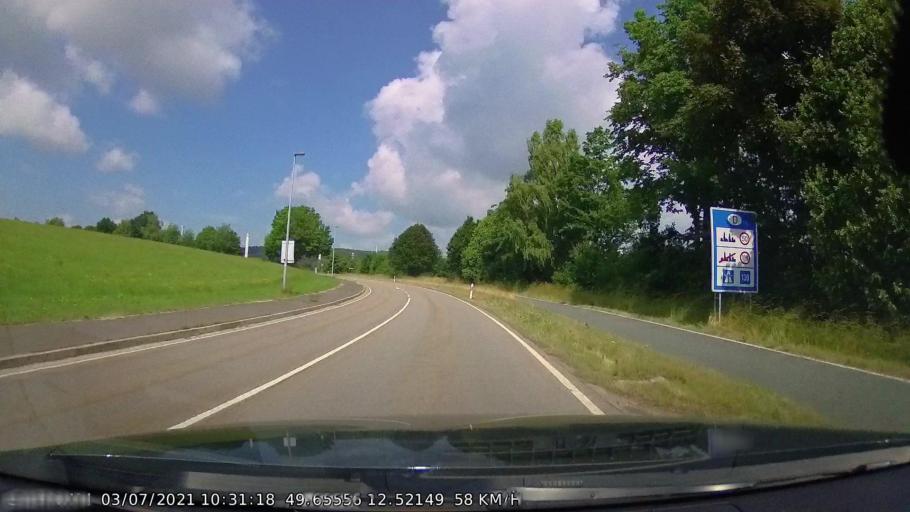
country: DE
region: Bavaria
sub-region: Upper Palatinate
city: Waidhaus
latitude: 49.6557
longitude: 12.5212
